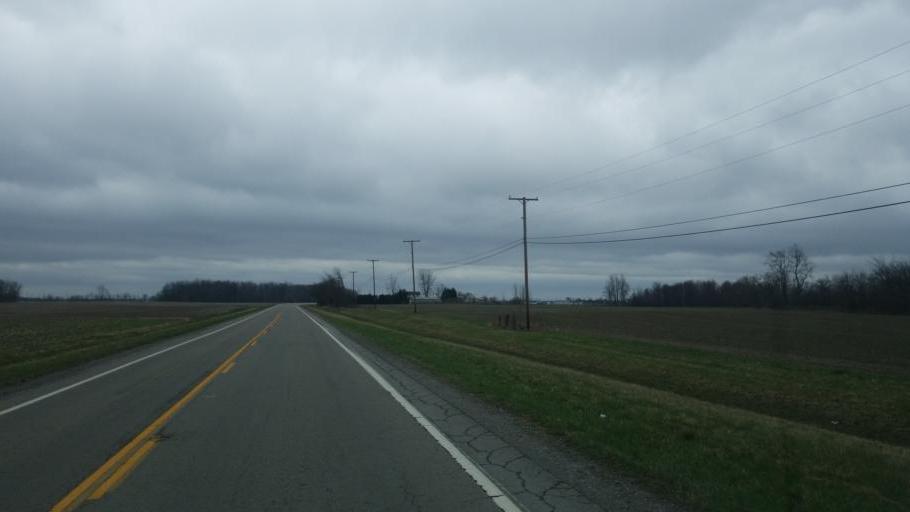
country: US
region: Ohio
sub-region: Hardin County
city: Forest
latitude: 40.7298
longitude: -83.5570
